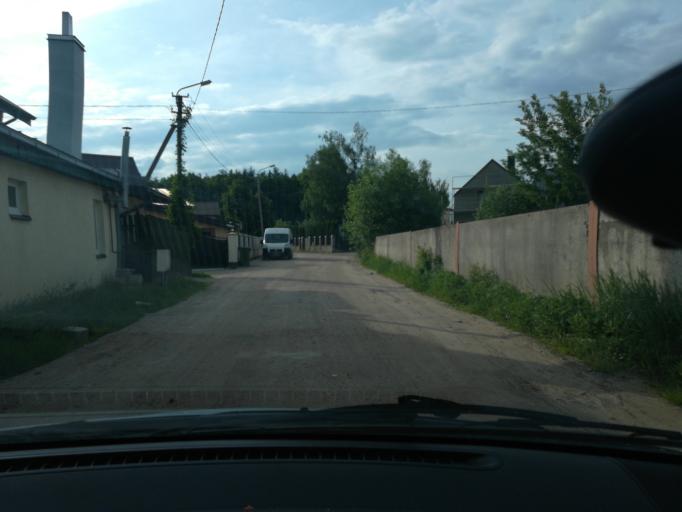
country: LT
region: Vilnius County
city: Rasos
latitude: 54.6648
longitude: 25.3418
